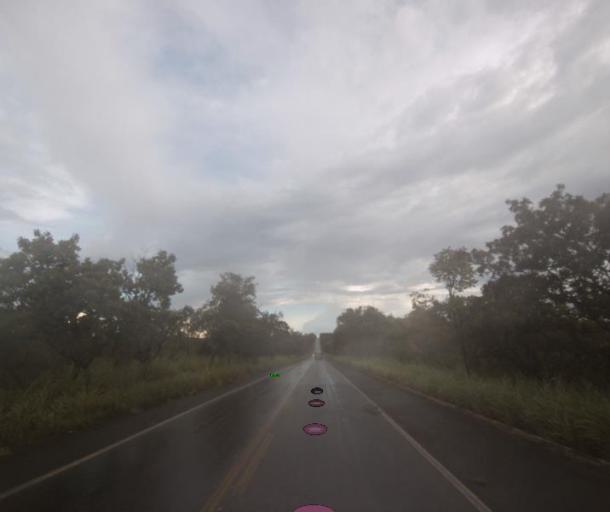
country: BR
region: Goias
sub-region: Porangatu
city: Porangatu
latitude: -13.8239
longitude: -49.0421
